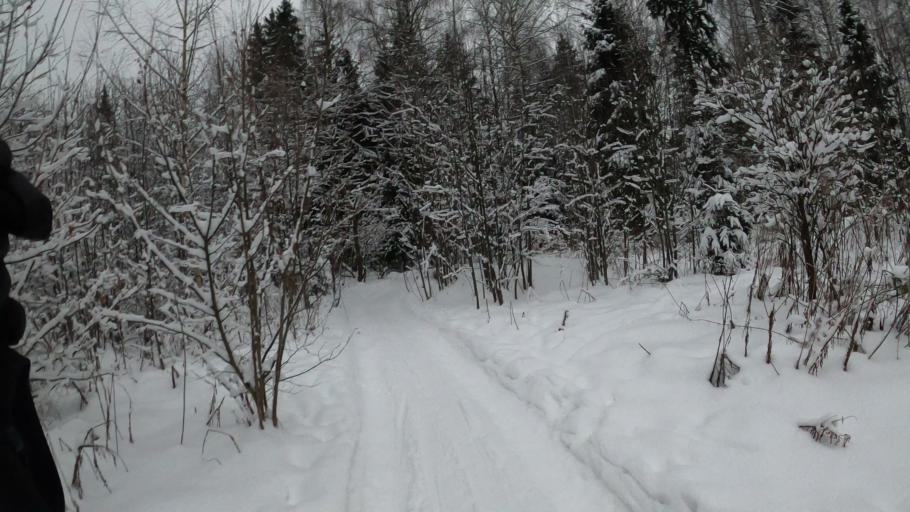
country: RU
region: Moskovskaya
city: Firsanovka
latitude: 55.9080
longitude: 37.2024
